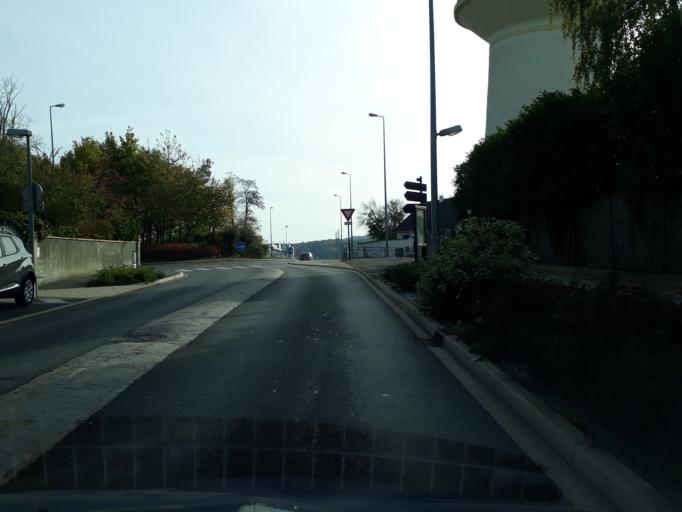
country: FR
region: Ile-de-France
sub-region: Departement de Seine-et-Marne
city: Samoreau
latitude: 48.4253
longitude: 2.7609
